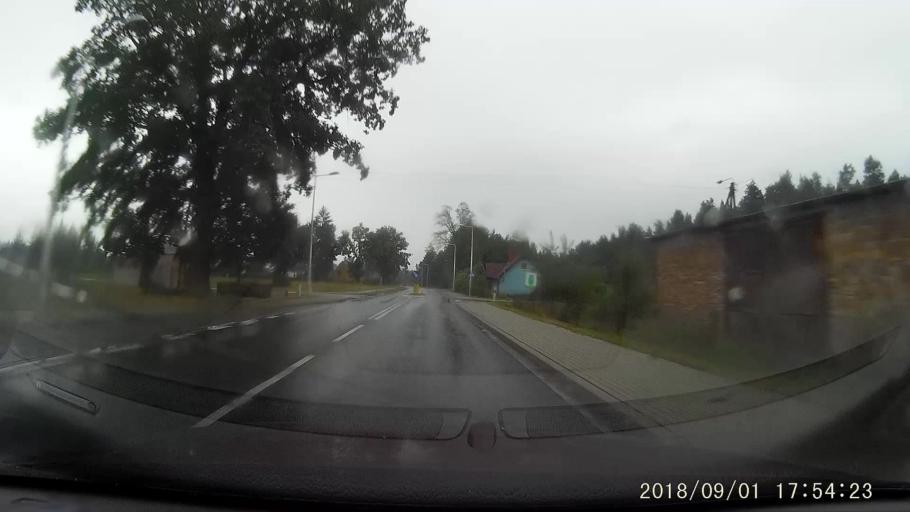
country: PL
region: Lubusz
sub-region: Powiat zaganski
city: Ilowa
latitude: 51.4693
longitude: 15.1994
